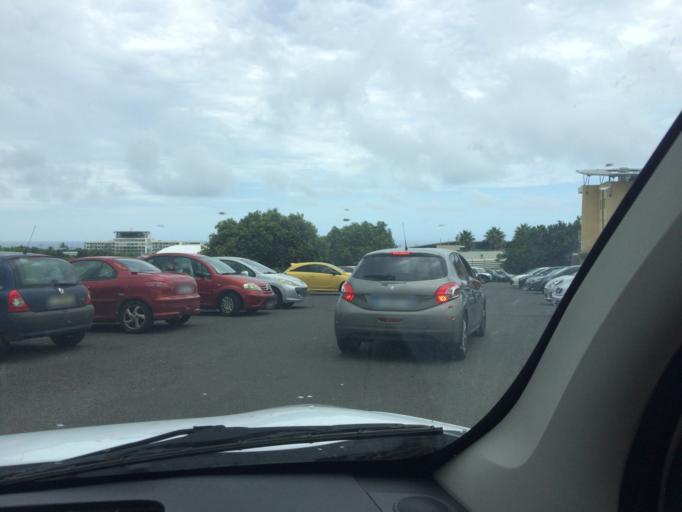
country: RE
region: Reunion
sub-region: Reunion
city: Saint-Pierre
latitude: -21.3403
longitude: 55.4913
